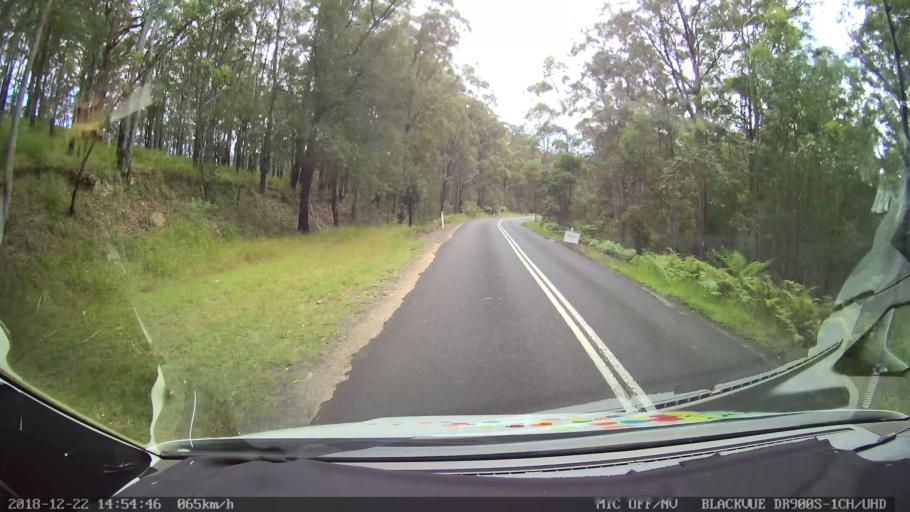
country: AU
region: New South Wales
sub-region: Bellingen
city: Dorrigo
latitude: -30.2281
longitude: 152.5290
